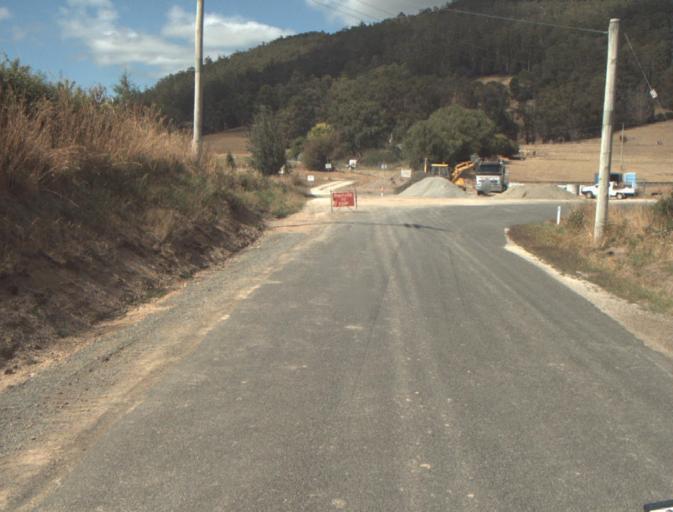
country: AU
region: Tasmania
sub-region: Launceston
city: Mayfield
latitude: -41.2594
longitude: 147.2074
